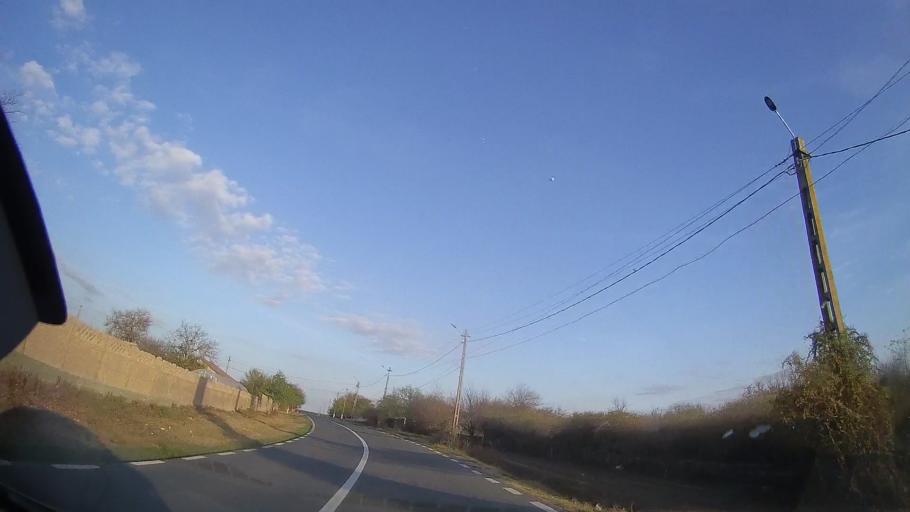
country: RO
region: Constanta
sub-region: Comuna Chirnogeni
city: Plopeni
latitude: 43.9506
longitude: 28.1857
